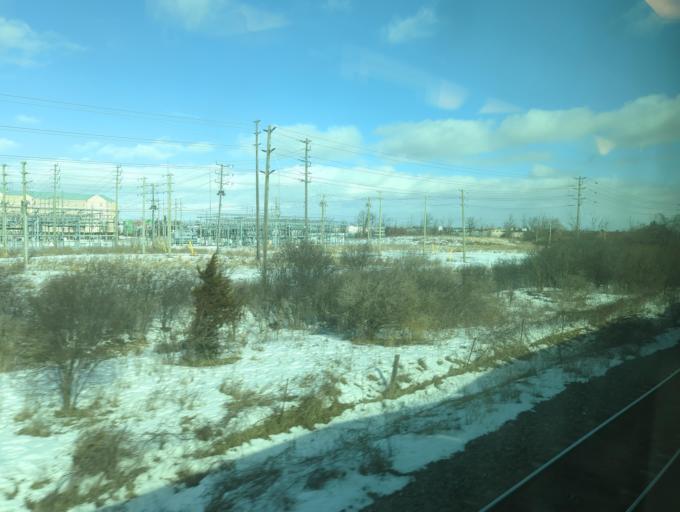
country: CA
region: Ontario
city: Oakville
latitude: 43.4061
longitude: -79.7334
